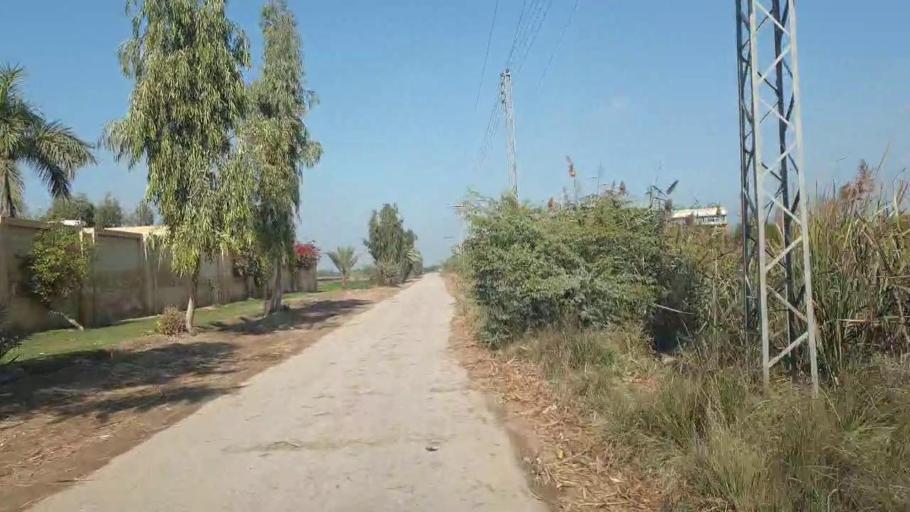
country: PK
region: Sindh
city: Shahdadpur
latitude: 25.9087
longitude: 68.5960
